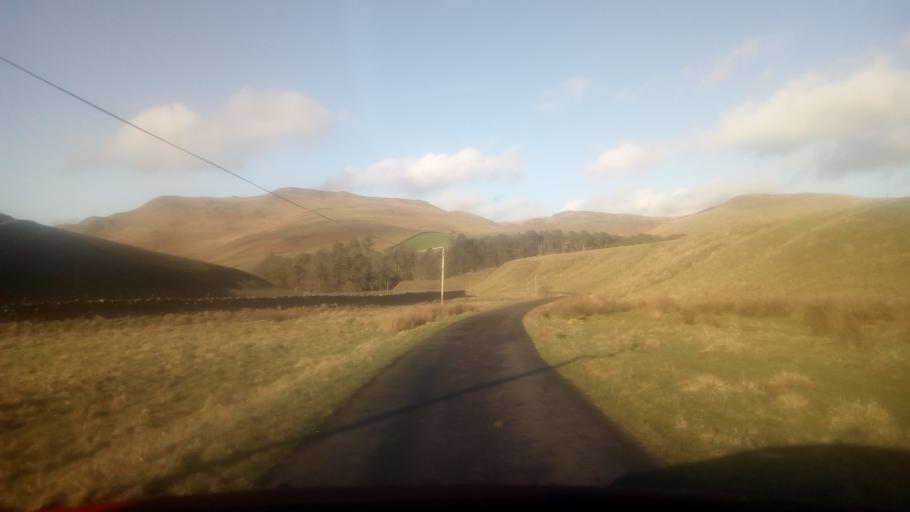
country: GB
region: England
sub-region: Northumberland
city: Rochester
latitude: 55.3840
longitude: -2.3759
